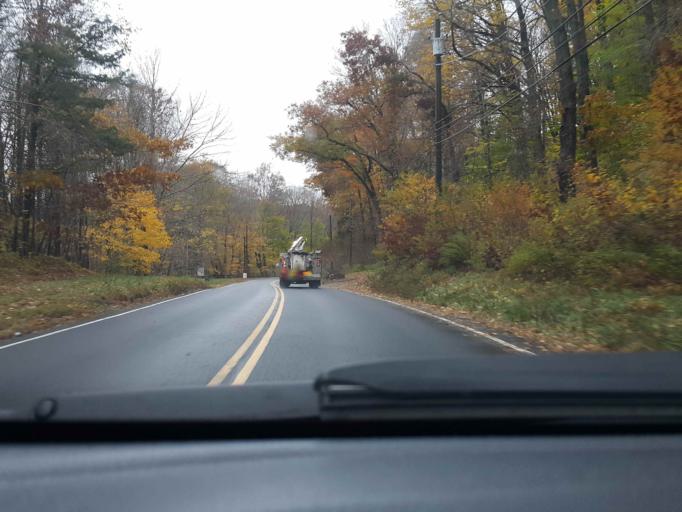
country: US
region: Connecticut
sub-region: Middlesex County
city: Durham
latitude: 41.4224
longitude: -72.6903
